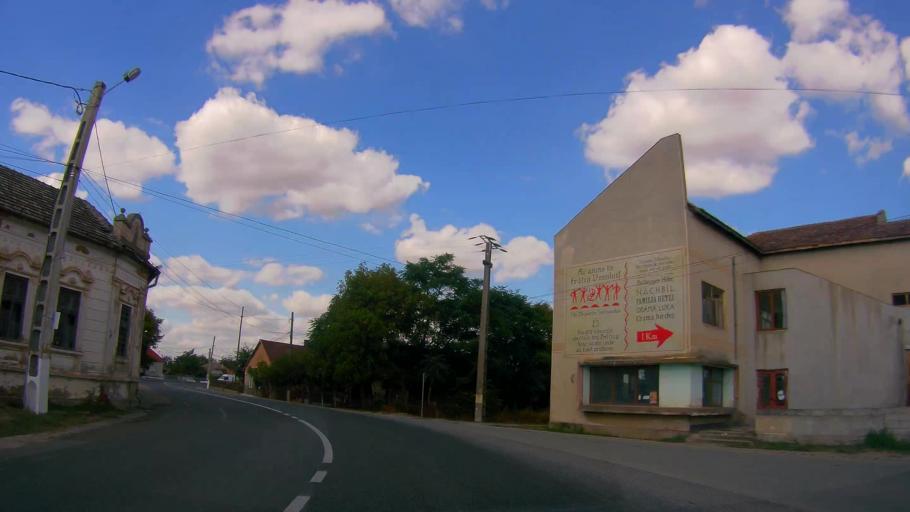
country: RO
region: Satu Mare
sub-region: Comuna Beltiug
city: Beltiug
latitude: 47.5488
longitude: 22.8412
